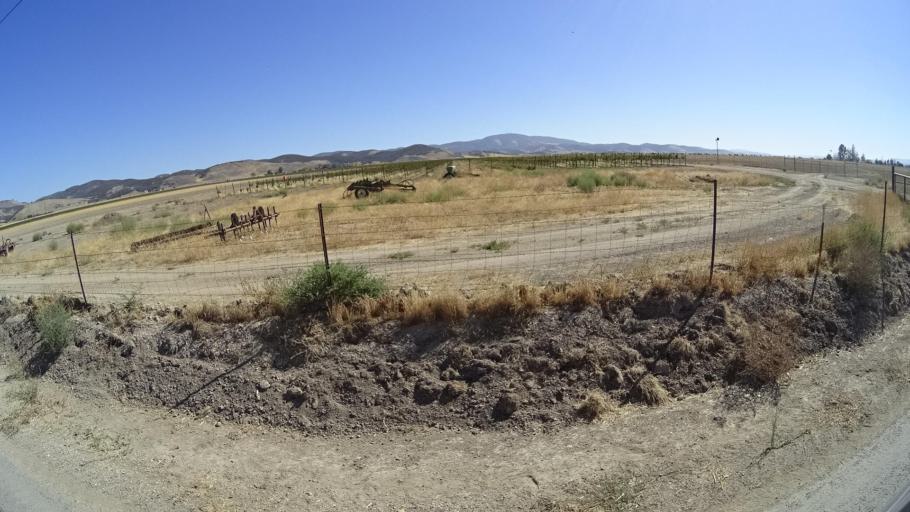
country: US
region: California
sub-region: Monterey County
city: King City
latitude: 35.9619
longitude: -121.1010
